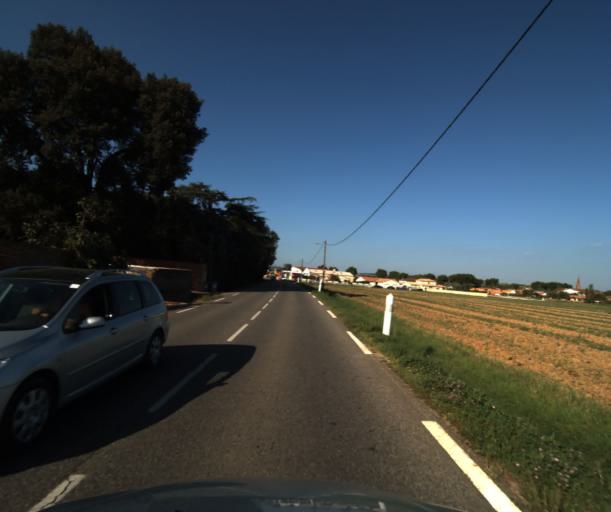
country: FR
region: Midi-Pyrenees
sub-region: Departement de la Haute-Garonne
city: Labarthe-sur-Leze
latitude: 43.4511
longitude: 1.3915
